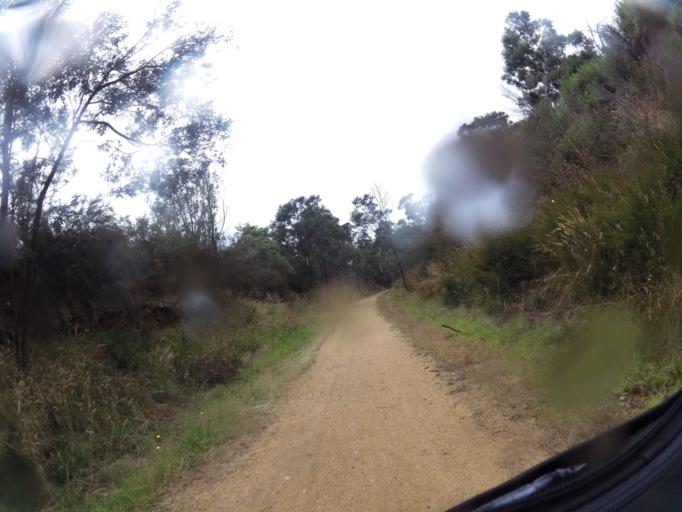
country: AU
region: Victoria
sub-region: East Gippsland
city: Lakes Entrance
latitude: -37.7624
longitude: 147.8201
